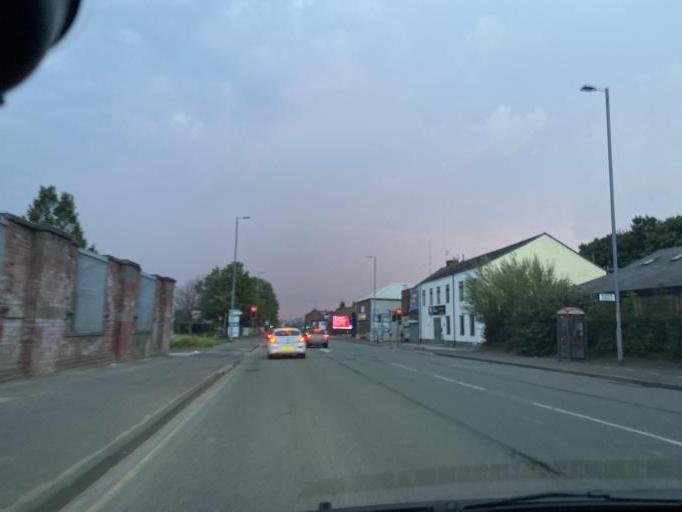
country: GB
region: England
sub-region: Manchester
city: Longsight
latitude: 53.4735
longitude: -2.1821
